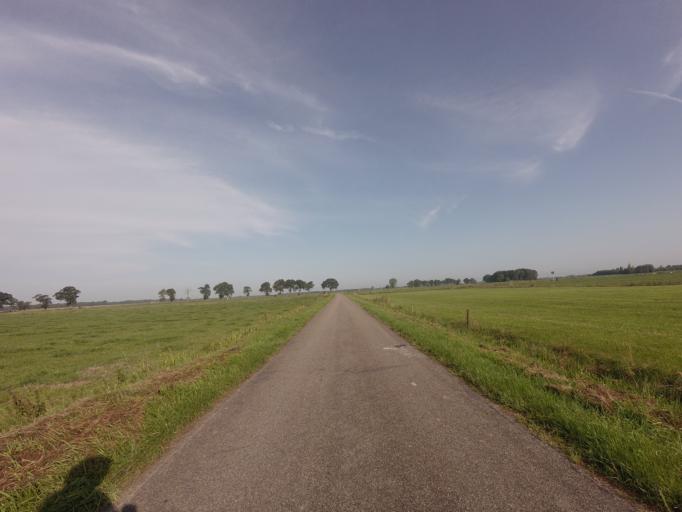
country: NL
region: Groningen
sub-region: Gemeente Leek
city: Leek
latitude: 53.1605
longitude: 6.4314
